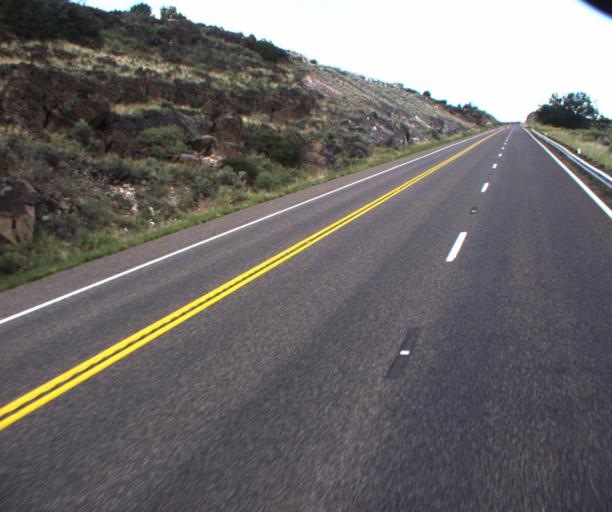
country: US
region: Arizona
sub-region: Apache County
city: Springerville
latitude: 34.1395
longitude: -109.2296
